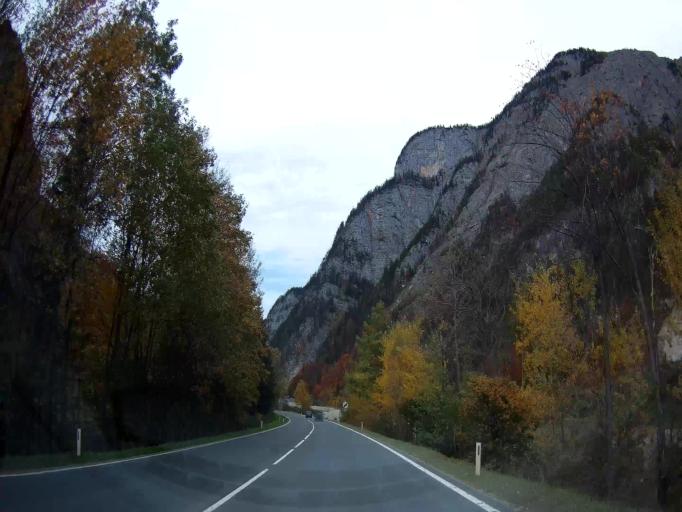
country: AT
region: Salzburg
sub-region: Politischer Bezirk Zell am See
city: Saalfelden am Steinernen Meer
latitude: 47.4876
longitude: 12.8246
